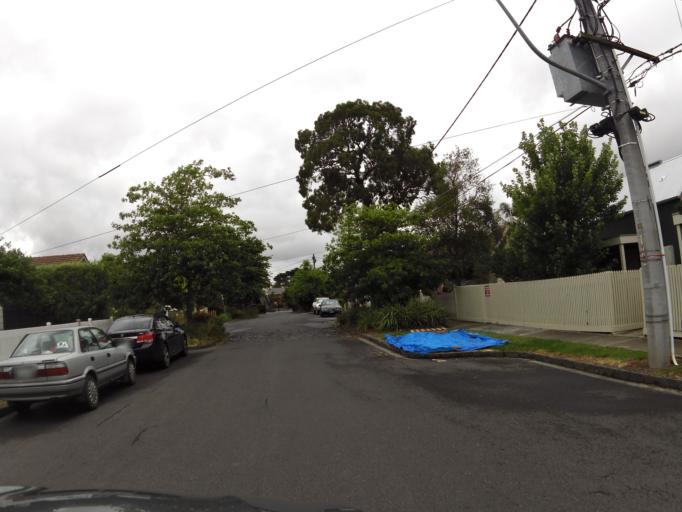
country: AU
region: Victoria
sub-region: Darebin
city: Fairfield
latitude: -37.7811
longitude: 145.0200
